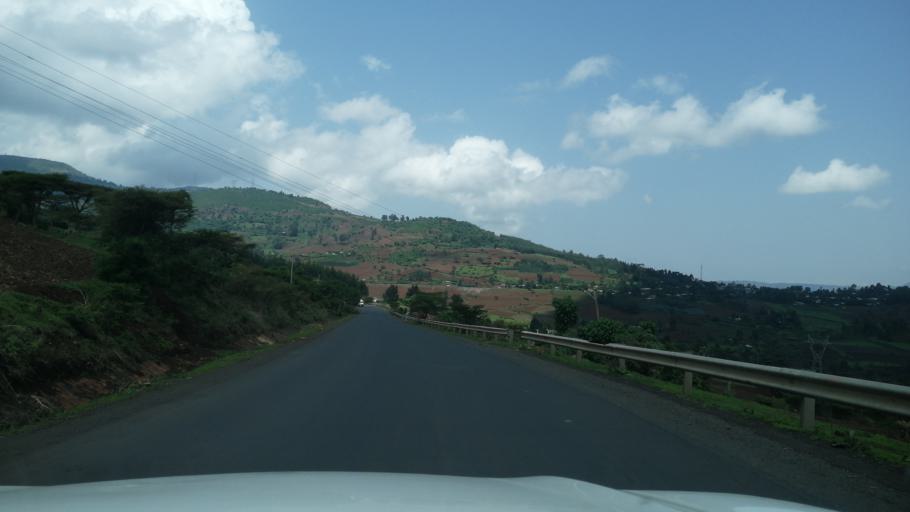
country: ET
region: Oromiya
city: Gedo
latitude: 8.9873
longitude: 37.6074
